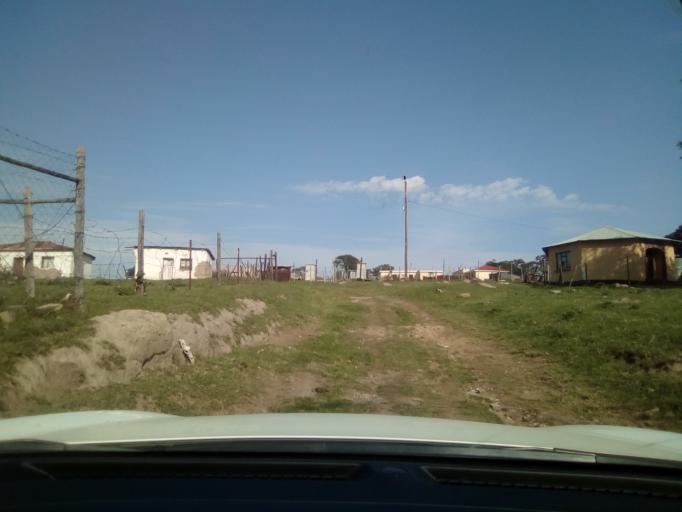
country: ZA
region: Eastern Cape
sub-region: Buffalo City Metropolitan Municipality
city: Bhisho
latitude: -32.9831
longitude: 27.2621
